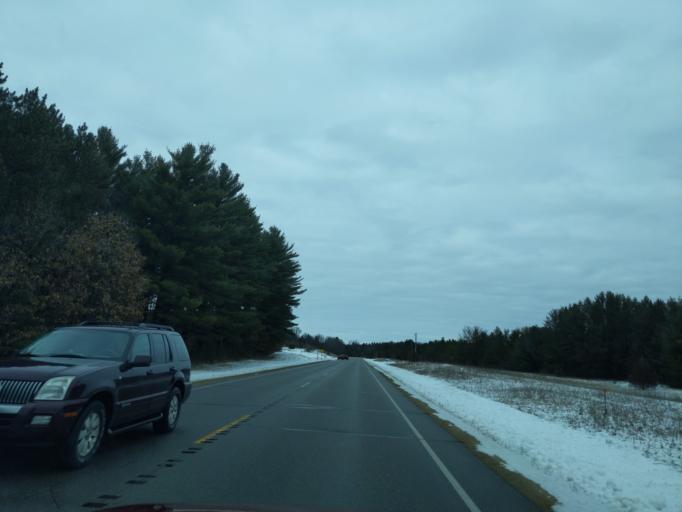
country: US
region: Wisconsin
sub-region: Waushara County
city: Wautoma
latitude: 43.9506
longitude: -89.3175
